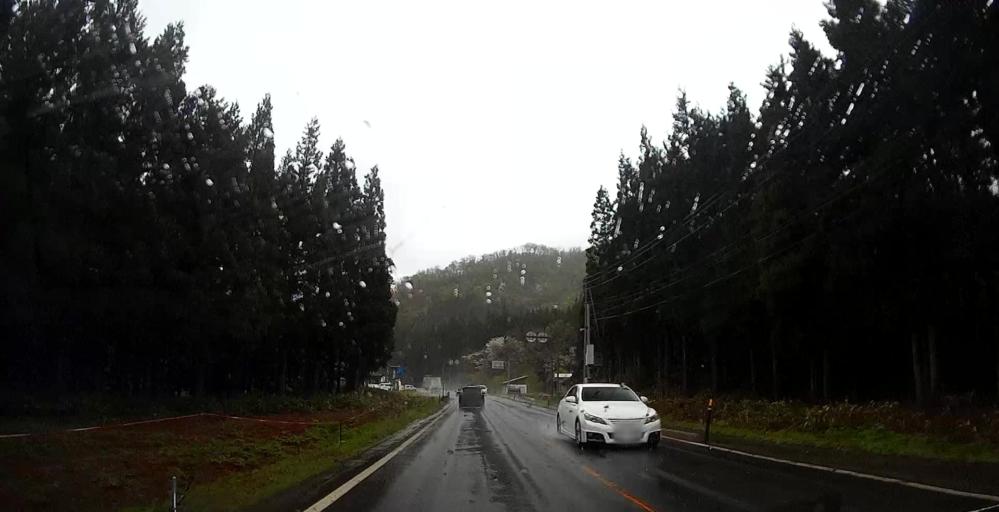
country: JP
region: Yamagata
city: Nagai
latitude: 38.0489
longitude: 139.8402
